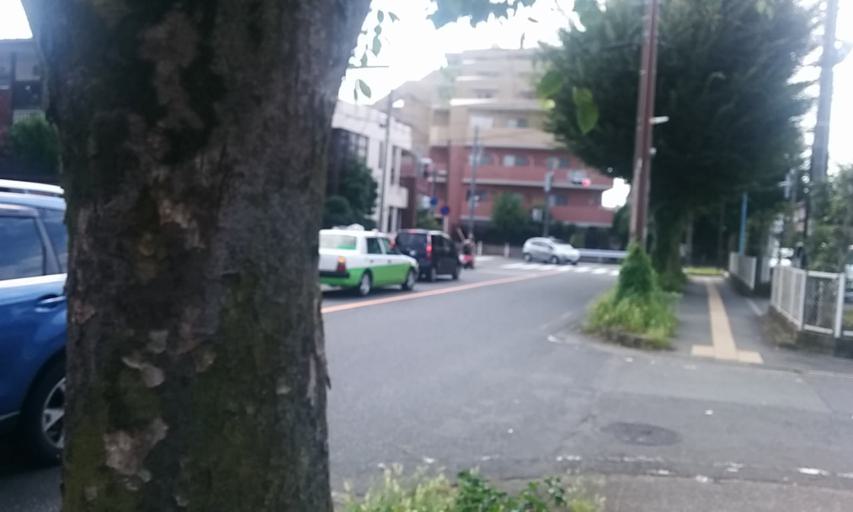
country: JP
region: Tokyo
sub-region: Machida-shi
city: Machida
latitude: 35.5631
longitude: 139.3982
